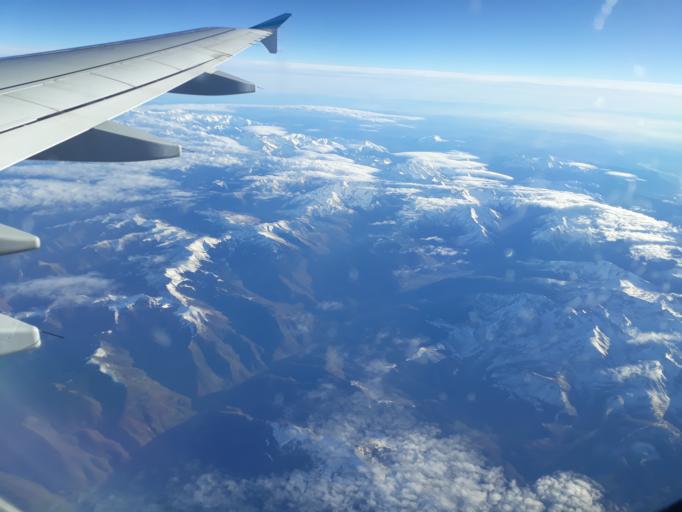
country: FR
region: Midi-Pyrenees
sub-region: Departement des Hautes-Pyrenees
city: Capvern
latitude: 43.0694
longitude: 0.2612
